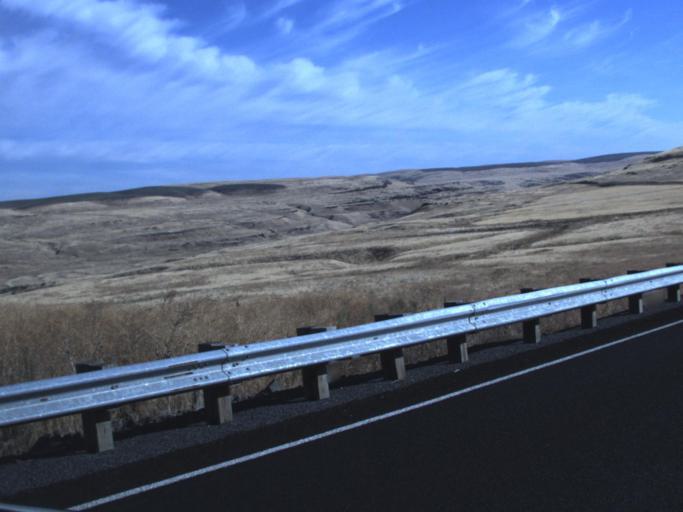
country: US
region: Washington
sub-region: Franklin County
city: Connell
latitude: 46.6226
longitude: -118.6556
